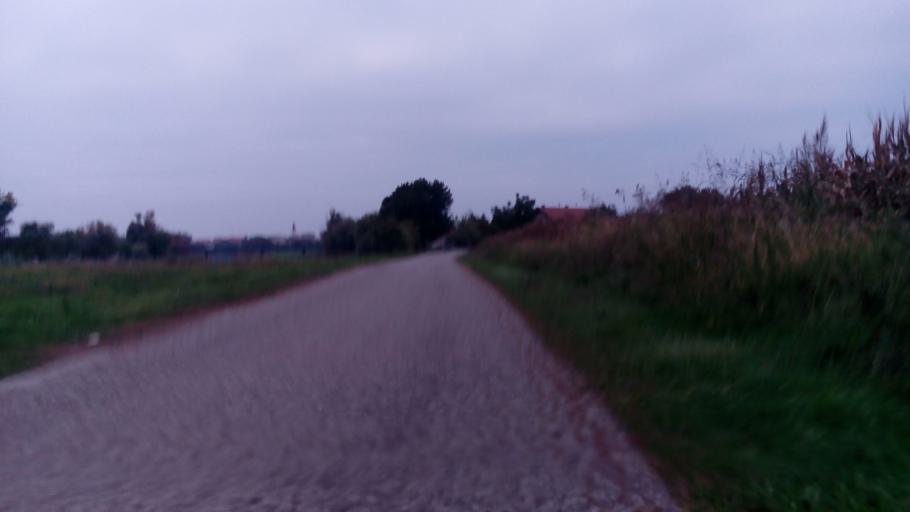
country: HR
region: Vukovarsko-Srijemska
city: Vinkovci
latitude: 45.2765
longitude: 18.8096
